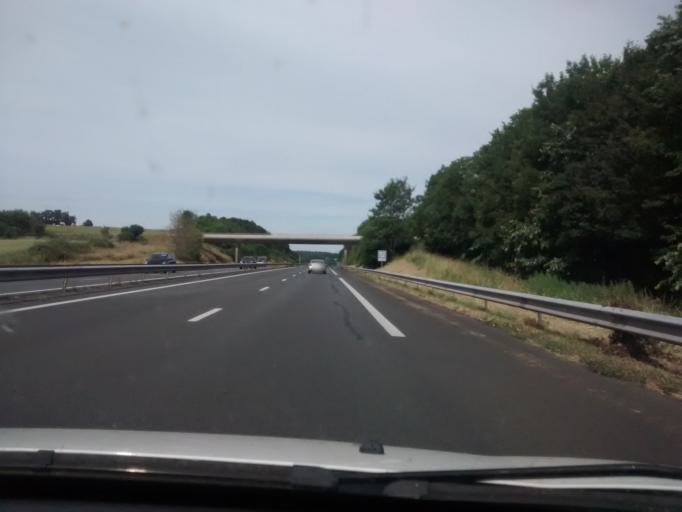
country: FR
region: Pays de la Loire
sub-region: Departement de la Sarthe
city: Saint-Georges-du-Bois
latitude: 47.9881
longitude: 0.0648
